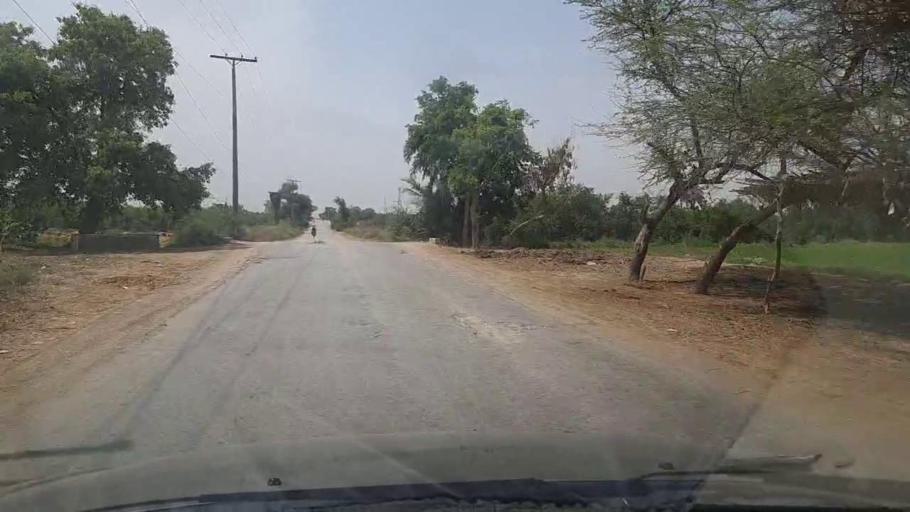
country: PK
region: Sindh
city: Bhiria
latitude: 26.9038
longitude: 68.2046
